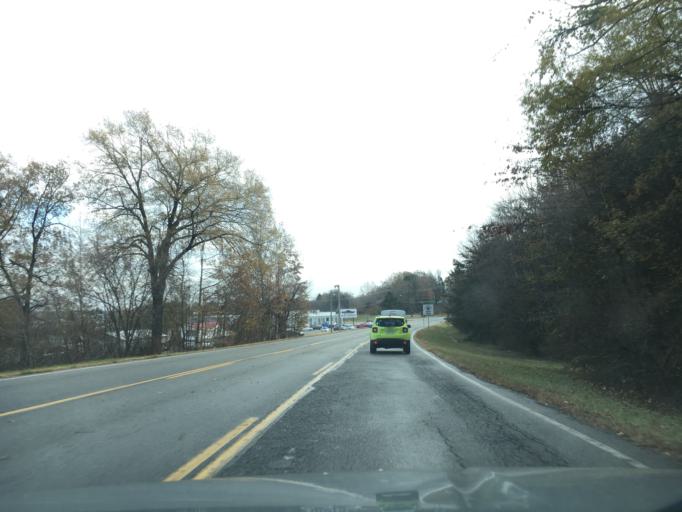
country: US
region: Virginia
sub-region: Prince Edward County
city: Farmville
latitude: 37.3143
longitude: -78.4243
